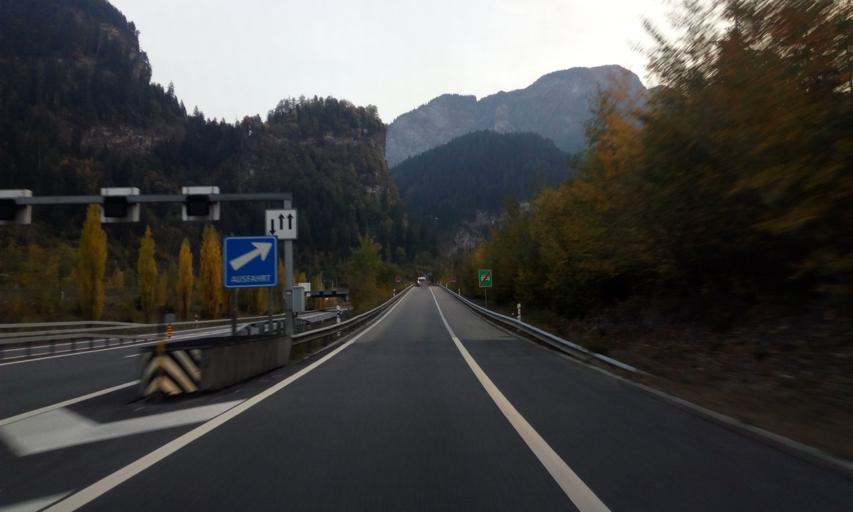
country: CH
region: Grisons
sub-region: Hinterrhein District
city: Thusis
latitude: 46.6994
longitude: 9.4466
